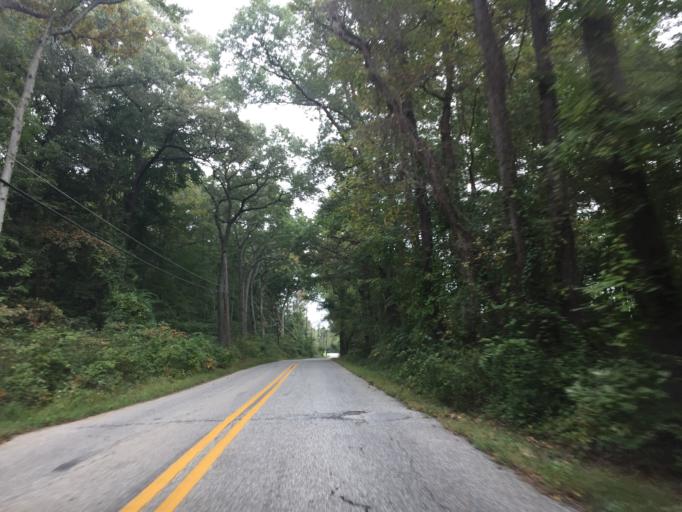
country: US
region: Maryland
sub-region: Baltimore County
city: Bowleys Quarters
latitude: 39.3656
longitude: -76.3883
